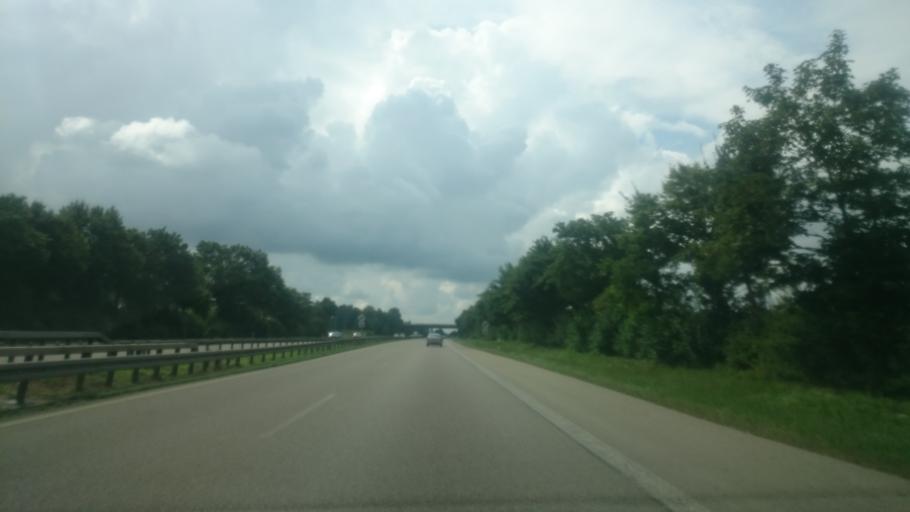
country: DE
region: Bavaria
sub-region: Swabia
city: Oberottmarshausen
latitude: 48.2512
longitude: 10.8683
